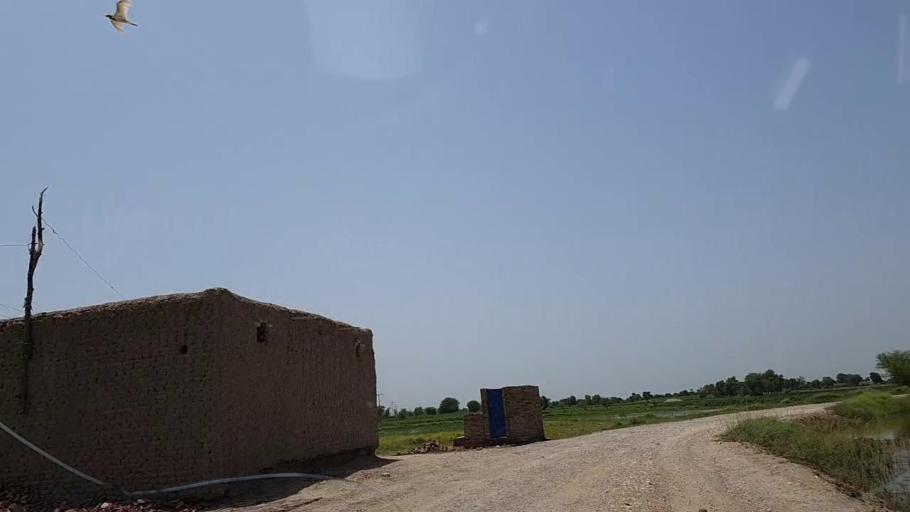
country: PK
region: Sindh
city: Tharu Shah
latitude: 26.9353
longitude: 68.0484
